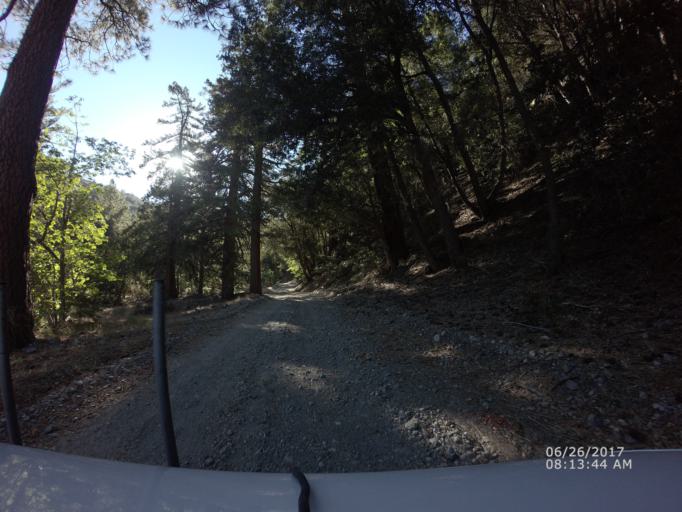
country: US
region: California
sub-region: San Bernardino County
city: Pinon Hills
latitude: 34.3823
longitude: -117.7701
